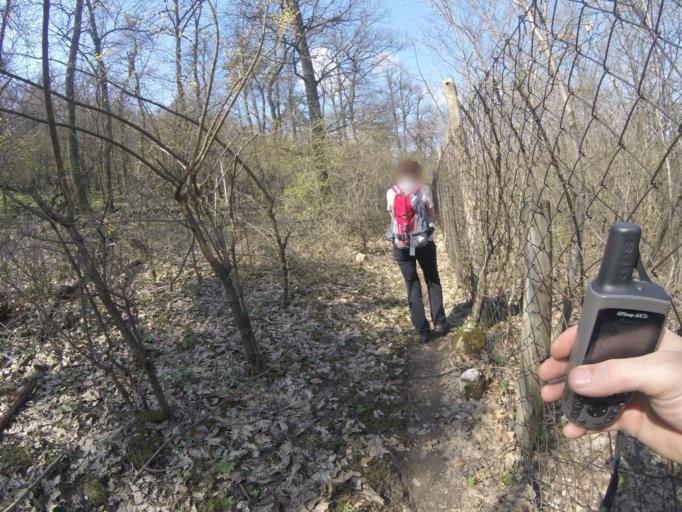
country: HU
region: Pest
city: Budakeszi
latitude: 47.5375
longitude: 18.9267
